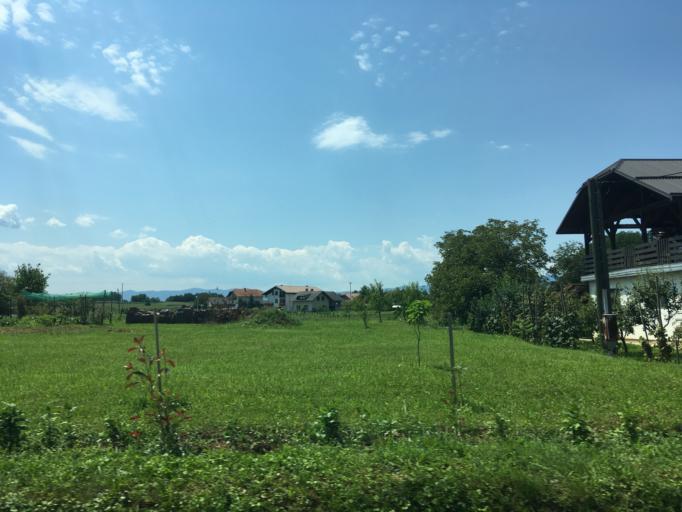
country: SI
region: Metlika
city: Metlika
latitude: 45.6199
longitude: 15.3220
